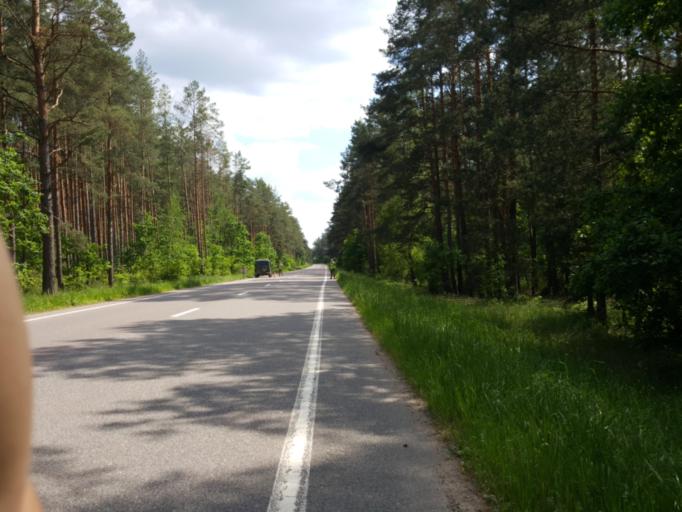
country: BY
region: Brest
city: Kamyanyuki
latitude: 52.5113
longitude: 23.6592
